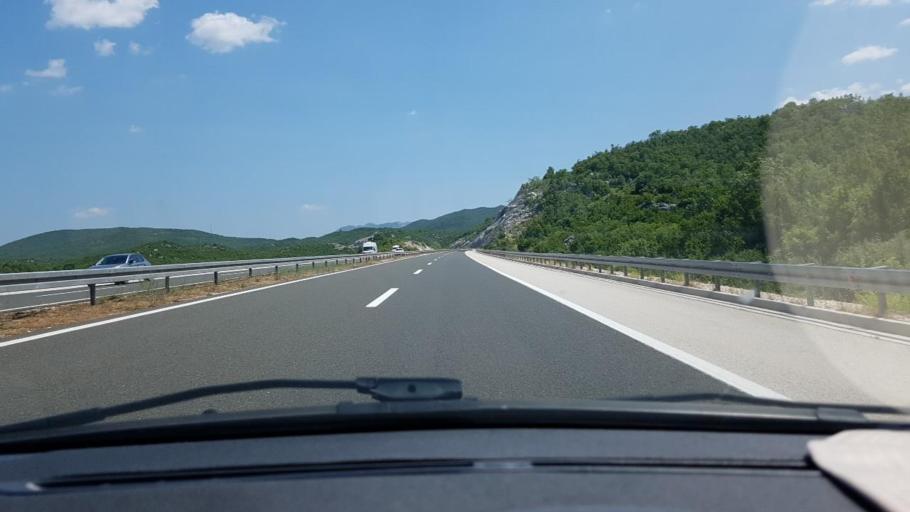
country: HR
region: Splitsko-Dalmatinska
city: Grubine
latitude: 43.3569
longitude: 17.1069
